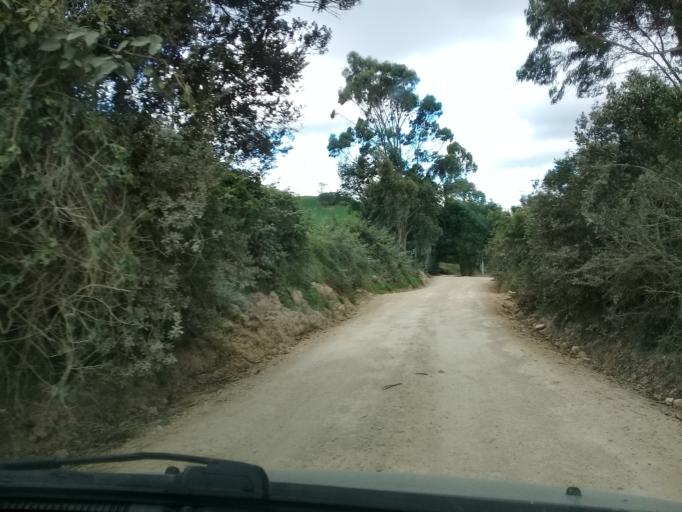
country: CO
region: Cundinamarca
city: Lenguazaque
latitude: 5.2878
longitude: -73.6810
